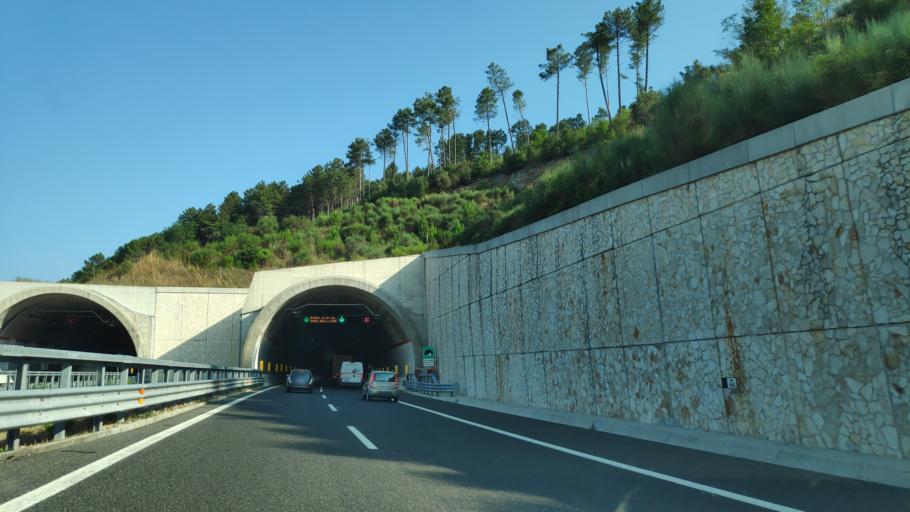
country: IT
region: Campania
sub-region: Provincia di Salerno
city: Casalbuono
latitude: 40.1867
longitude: 15.7084
